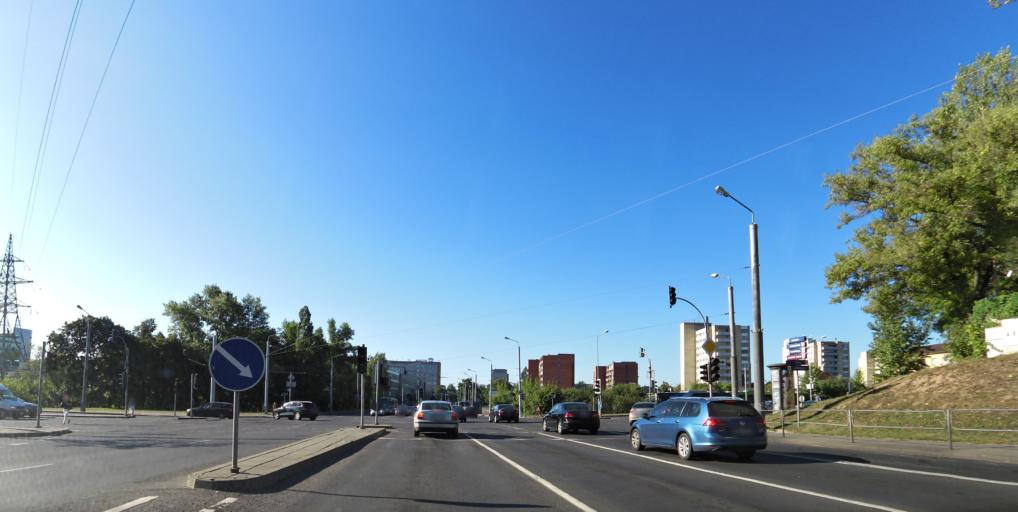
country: LT
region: Vilnius County
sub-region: Vilnius
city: Vilnius
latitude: 54.7155
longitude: 25.2868
